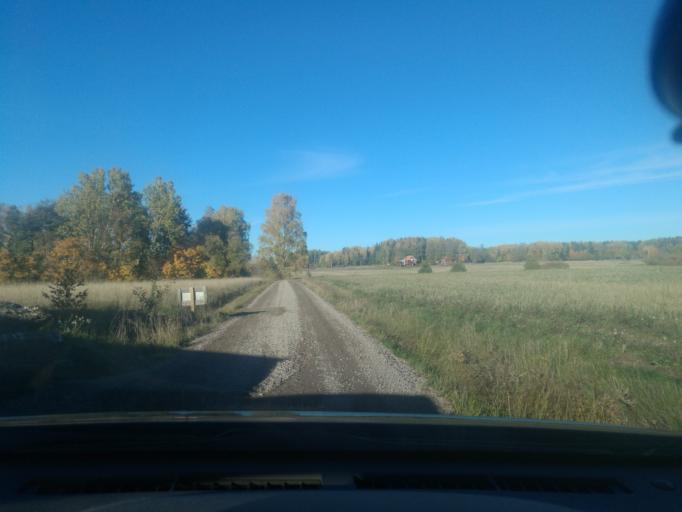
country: SE
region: Vaestmanland
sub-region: Kopings Kommun
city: Koping
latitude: 59.5942
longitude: 16.0070
